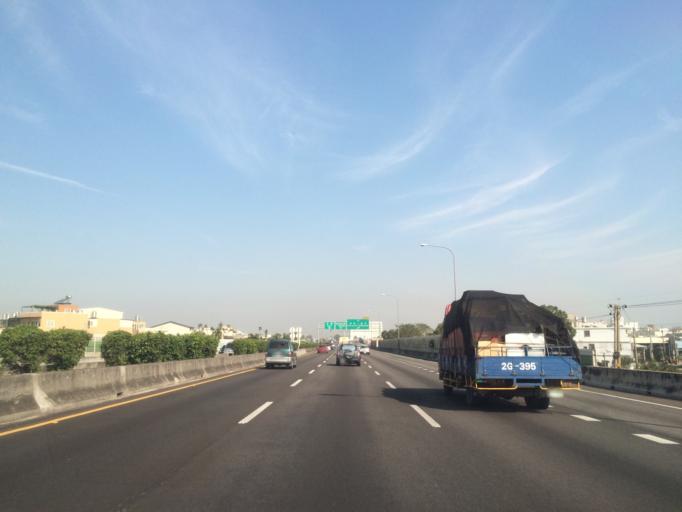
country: TW
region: Taiwan
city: Fengyuan
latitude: 24.2407
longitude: 120.6893
